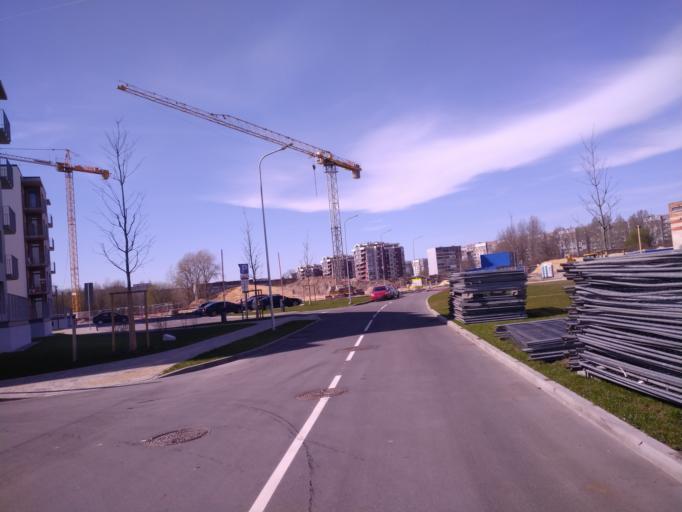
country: LV
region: Stopini
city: Ulbroka
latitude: 56.9386
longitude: 24.2253
